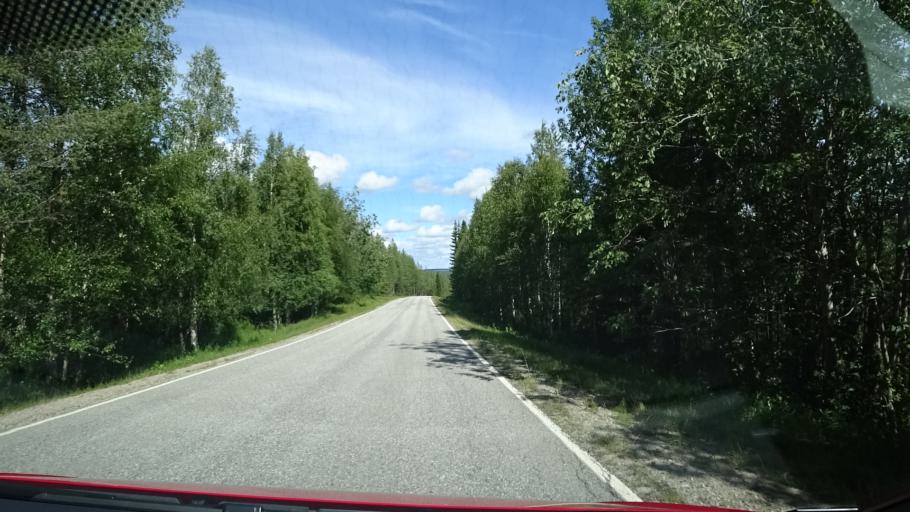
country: FI
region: Kainuu
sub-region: Kehys-Kainuu
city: Kuhmo
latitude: 64.6776
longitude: 29.6708
